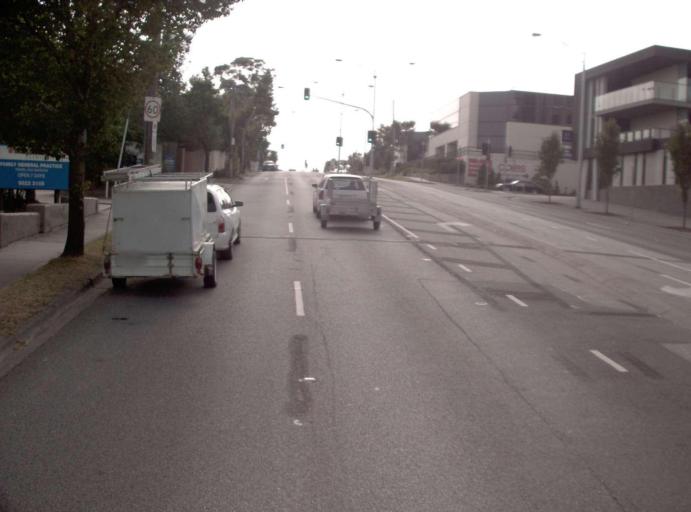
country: AU
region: Victoria
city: Glenferrie
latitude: -37.8453
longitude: 145.0458
